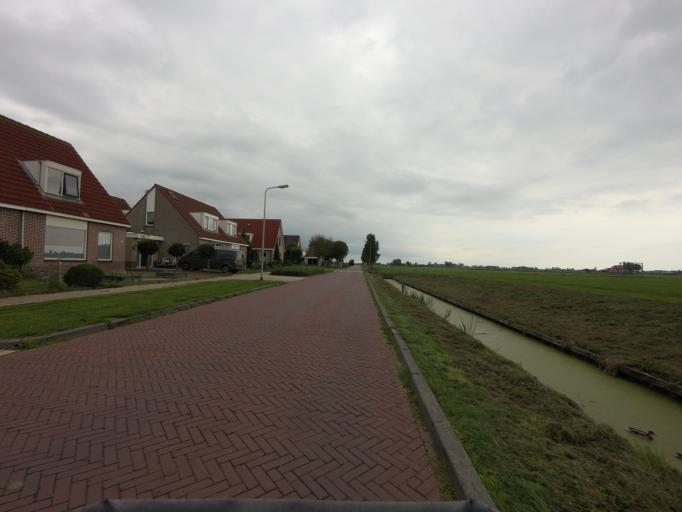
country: NL
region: Friesland
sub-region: Sudwest Fryslan
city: IJlst
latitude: 53.0181
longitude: 5.5988
